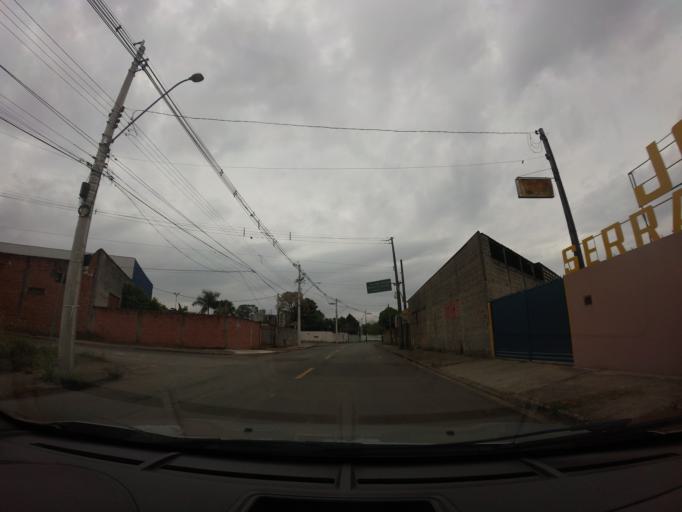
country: BR
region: Sao Paulo
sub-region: Piracicaba
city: Piracicaba
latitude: -22.7453
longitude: -47.5931
